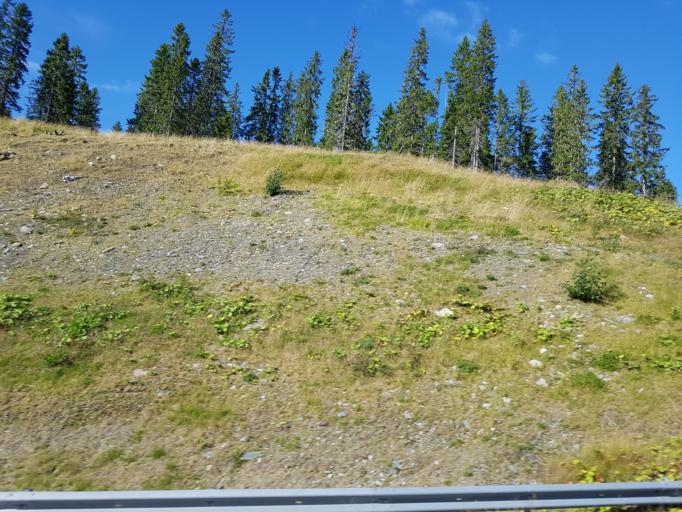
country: NO
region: Sor-Trondelag
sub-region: Trondheim
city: Trondheim
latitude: 63.6565
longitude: 10.2451
